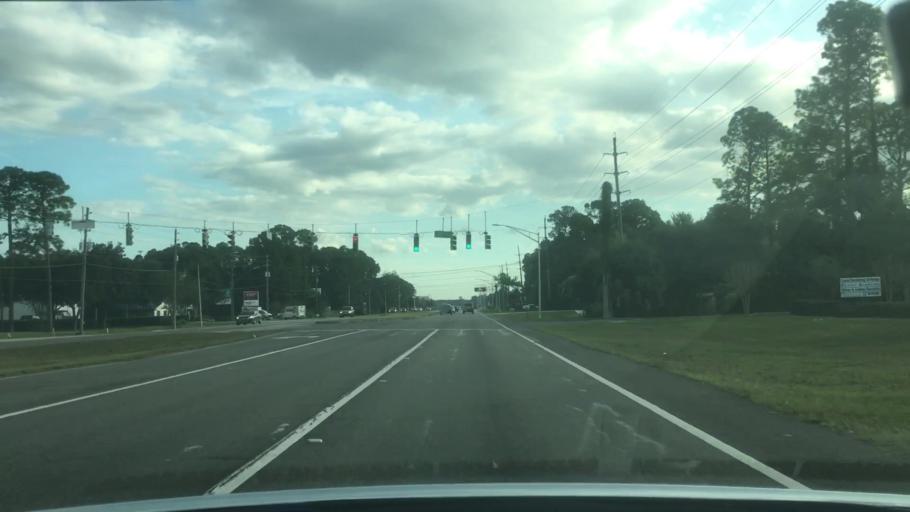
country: US
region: Florida
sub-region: Duval County
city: Neptune Beach
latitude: 30.2953
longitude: -81.5260
